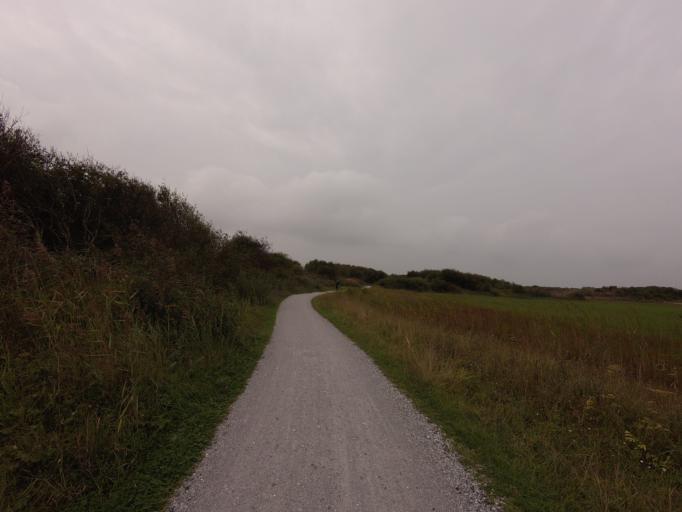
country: NL
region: Friesland
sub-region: Gemeente Schiermonnikoog
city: Schiermonnikoog
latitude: 53.4946
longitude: 6.1942
